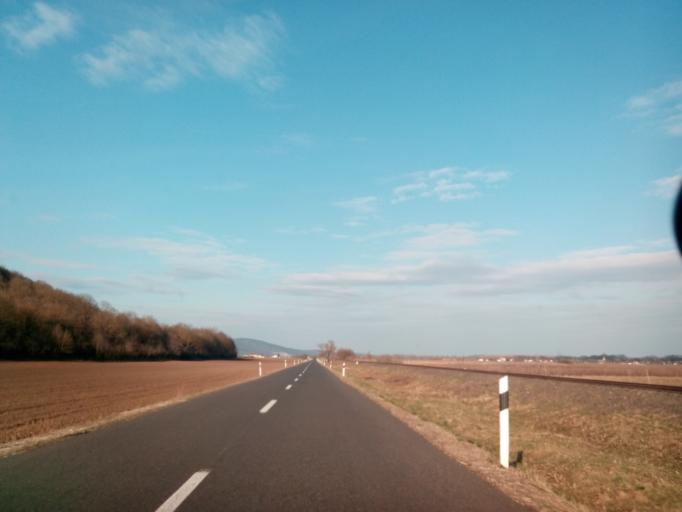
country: SK
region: Kosicky
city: Medzev
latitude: 48.5703
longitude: 20.8289
